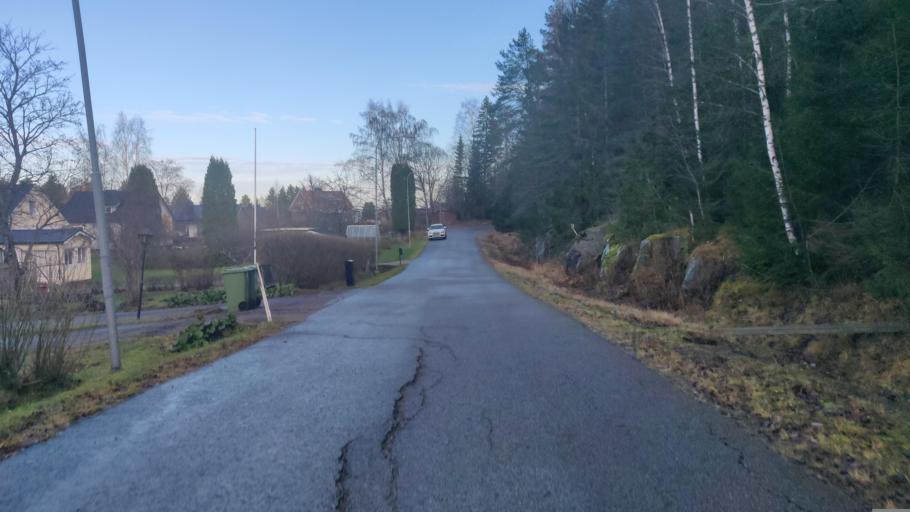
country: SE
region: Vaesternorrland
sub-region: Sundsvalls Kommun
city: Kvissleby
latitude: 62.3075
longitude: 17.3598
